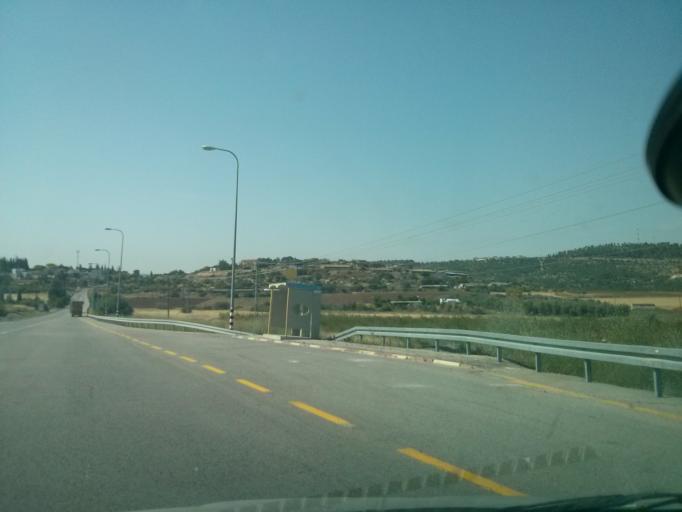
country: IL
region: Jerusalem
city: Bet Shemesh
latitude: 31.6812
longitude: 35.0033
